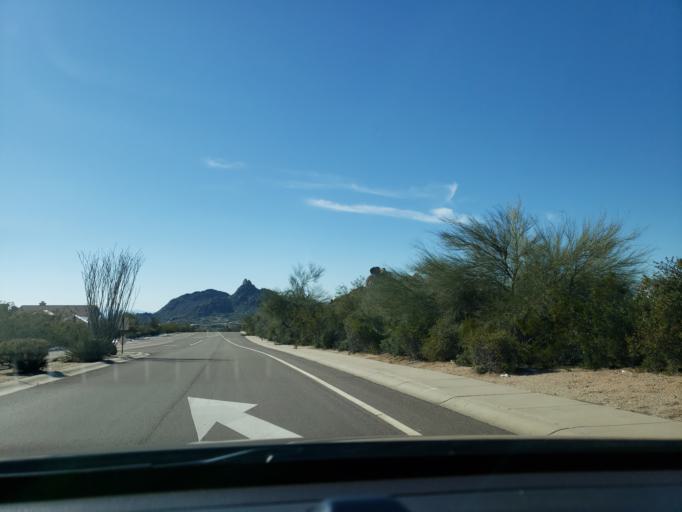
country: US
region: Arizona
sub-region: Maricopa County
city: Carefree
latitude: 33.7269
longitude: -111.8359
